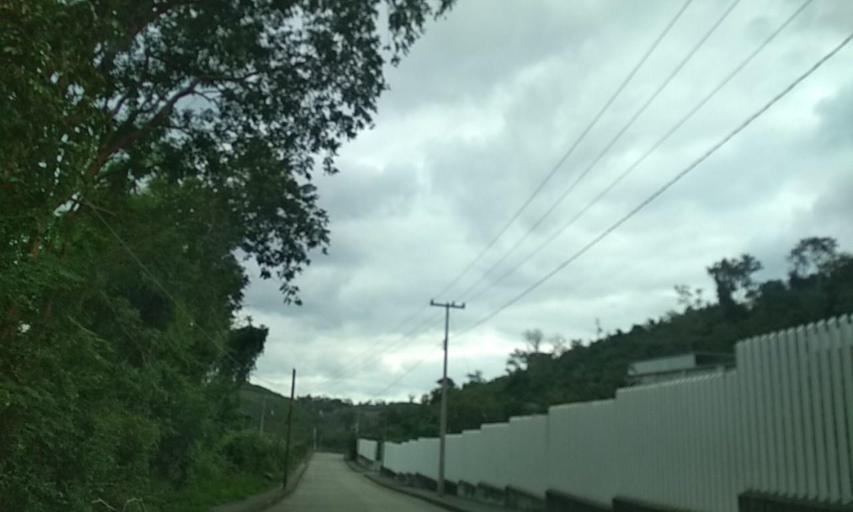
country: MX
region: Veracruz
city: Papantla de Olarte
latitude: 20.4734
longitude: -97.3206
